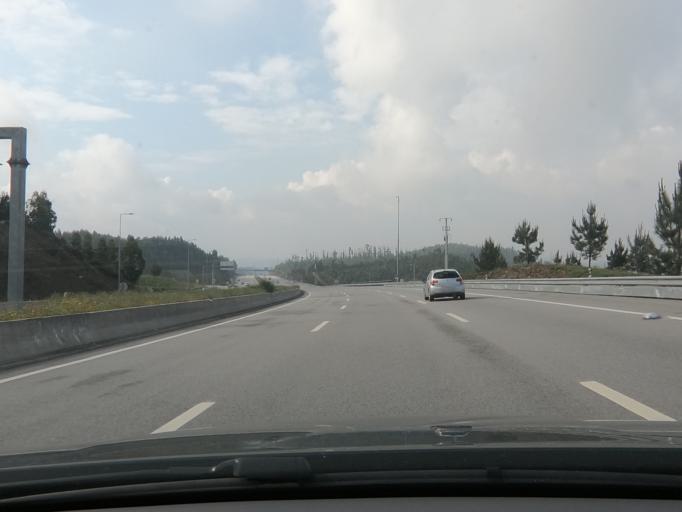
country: PT
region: Porto
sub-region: Gondomar
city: Foz do Sousa
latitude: 41.0967
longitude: -8.4574
